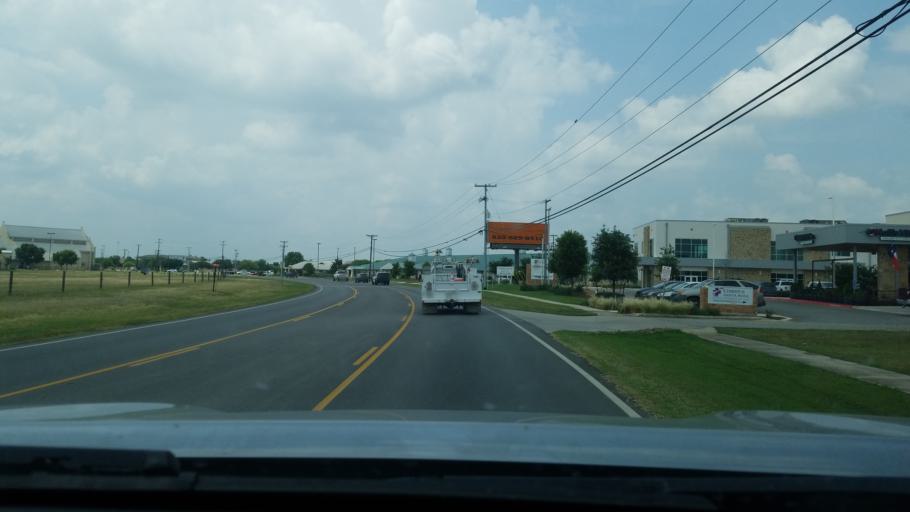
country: US
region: Texas
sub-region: Comal County
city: New Braunfels
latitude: 29.7269
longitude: -98.0951
